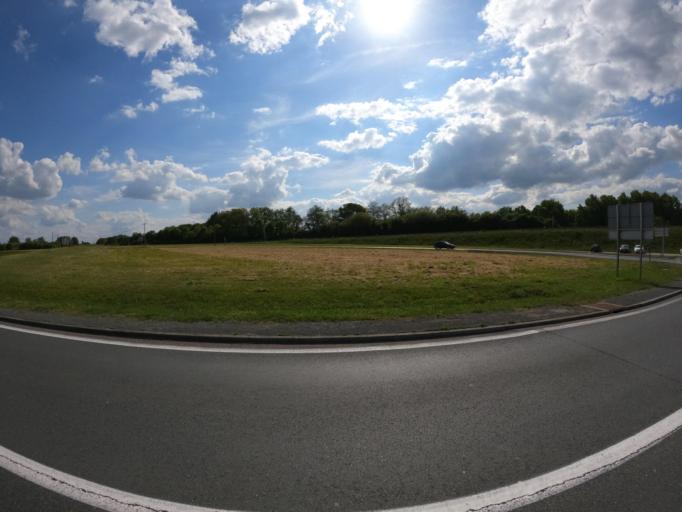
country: FR
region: Pays de la Loire
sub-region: Departement de Maine-et-Loire
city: La Tessoualle
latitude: 47.0203
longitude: -0.8822
